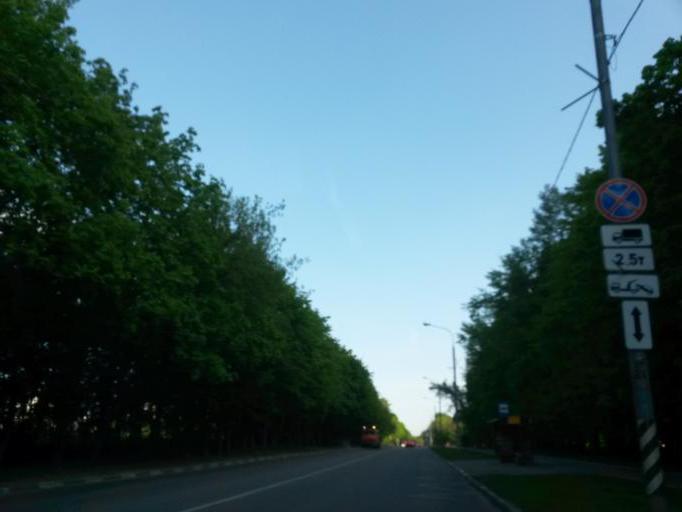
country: RU
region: Moskovskaya
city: Biryulevo Zapadnoye
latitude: 55.5890
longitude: 37.6554
